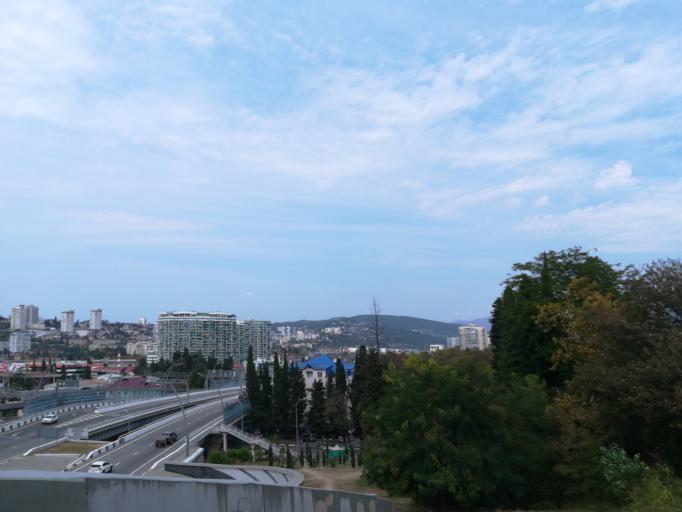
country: RU
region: Krasnodarskiy
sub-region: Sochi City
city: Sochi
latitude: 43.5897
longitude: 39.7308
